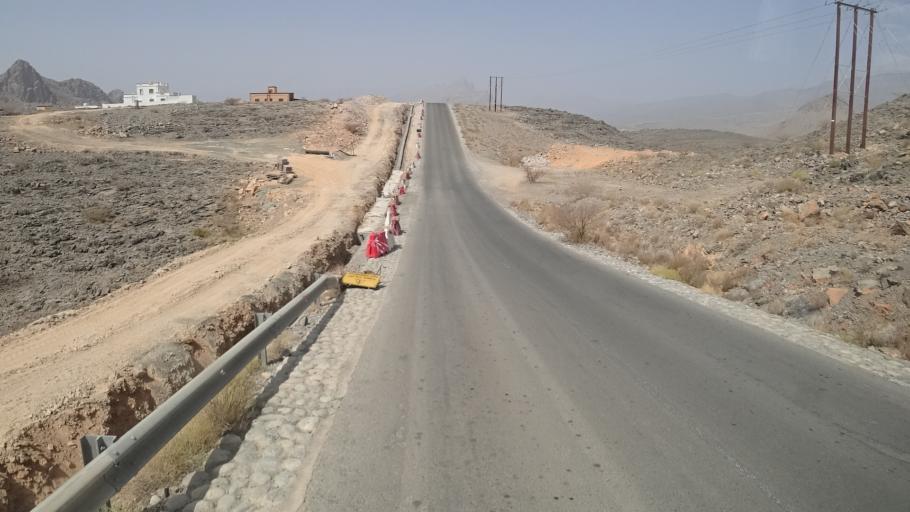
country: OM
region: Muhafazat ad Dakhiliyah
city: Bahla'
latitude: 23.0901
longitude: 57.3307
